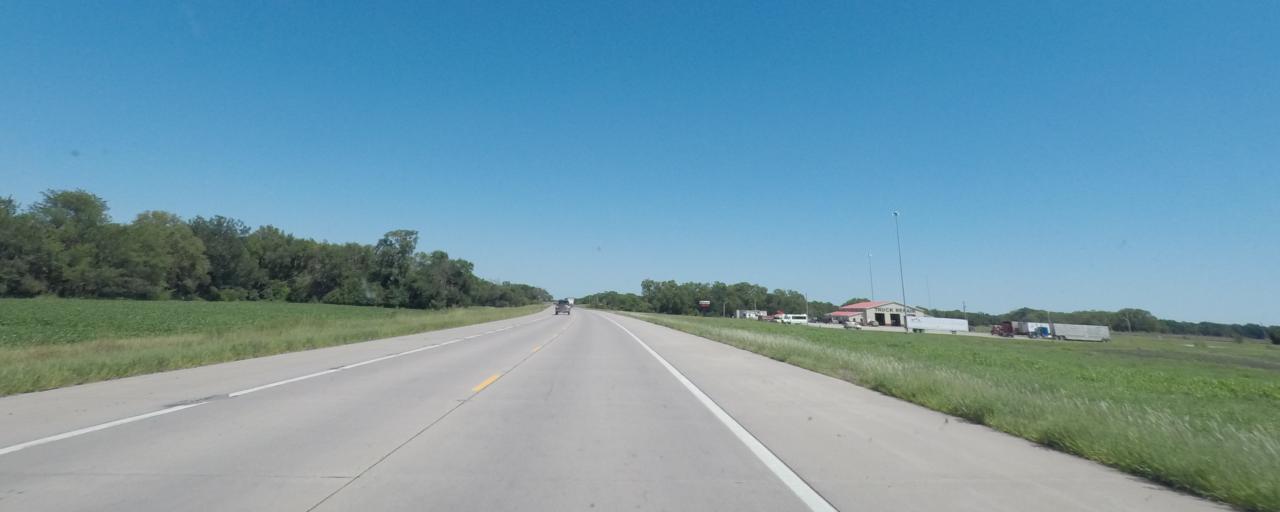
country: US
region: Kansas
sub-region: Lyon County
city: Emporia
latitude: 38.4068
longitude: -96.3064
